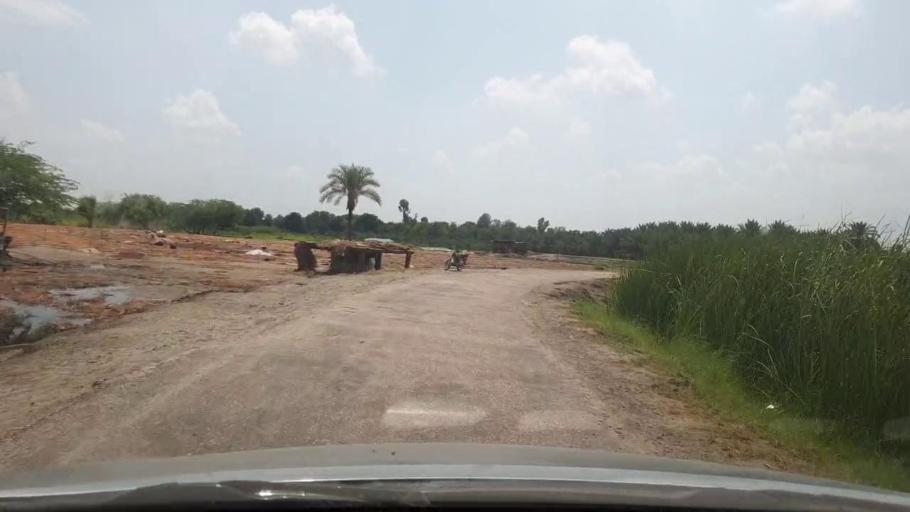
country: PK
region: Sindh
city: Kot Diji
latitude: 27.3961
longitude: 68.7320
